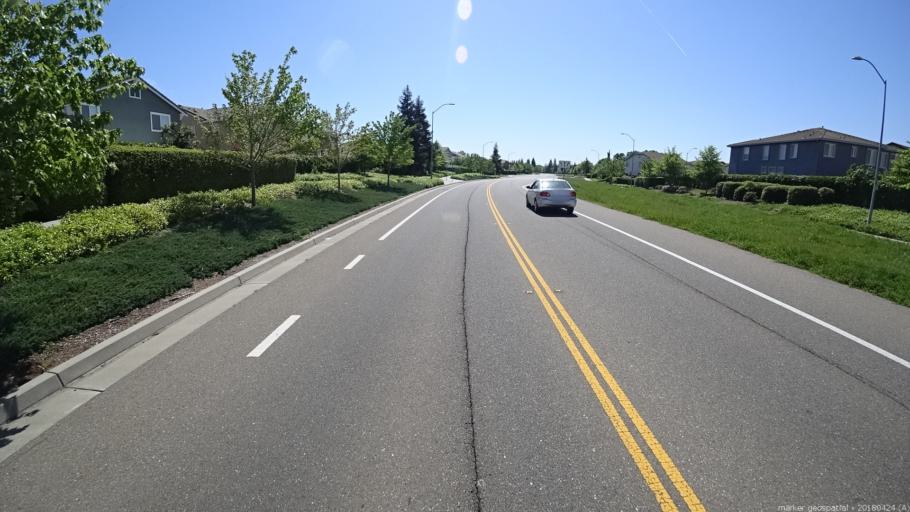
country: US
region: California
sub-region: Yolo County
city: West Sacramento
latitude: 38.5504
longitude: -121.5294
